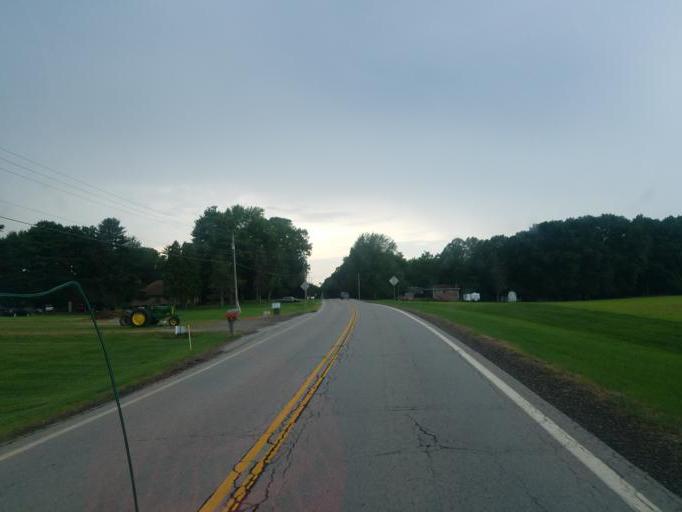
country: US
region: Ohio
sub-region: Wayne County
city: Rittman
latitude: 40.9463
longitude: -81.7656
